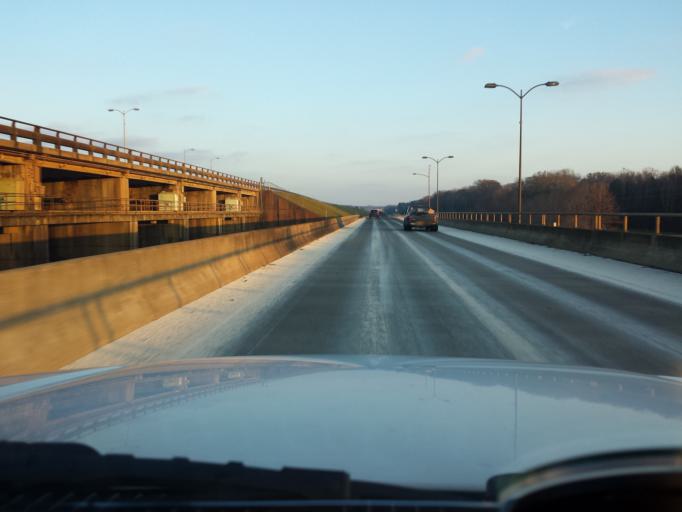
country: US
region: Mississippi
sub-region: Madison County
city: Ridgeland
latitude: 32.3971
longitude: -90.0644
